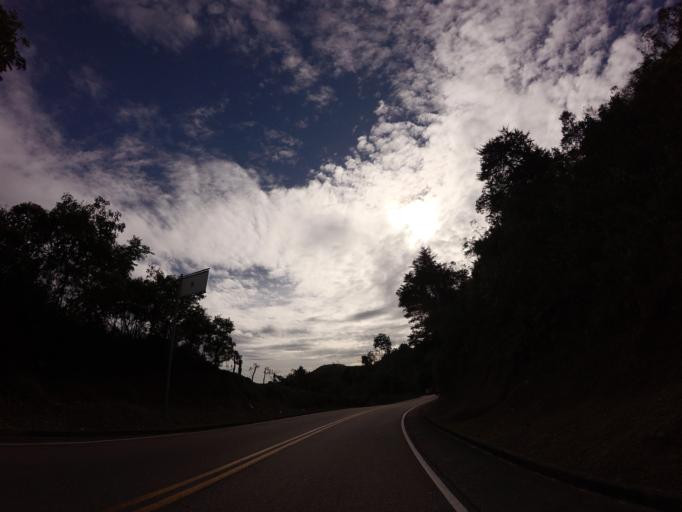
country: CO
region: Tolima
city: Casabianca
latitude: 5.1379
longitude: -75.1304
